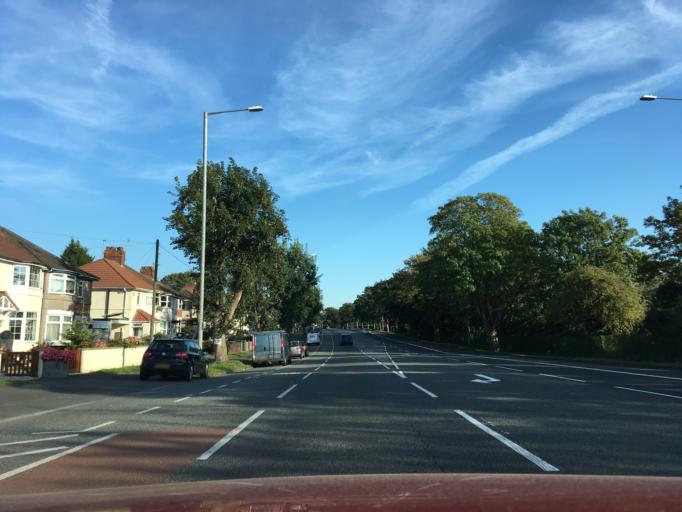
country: GB
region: England
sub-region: North Somerset
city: Easton-in-Gordano
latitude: 51.4888
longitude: -2.6863
